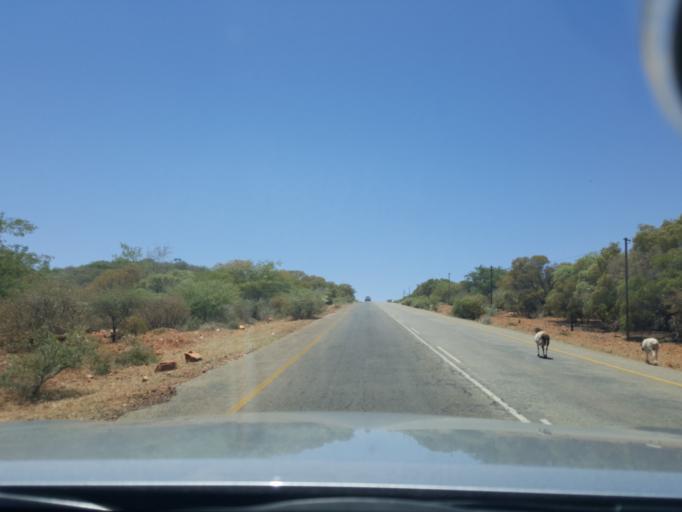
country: ZA
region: North-West
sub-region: Ngaka Modiri Molema District Municipality
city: Zeerust
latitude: -25.3128
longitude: 25.9335
